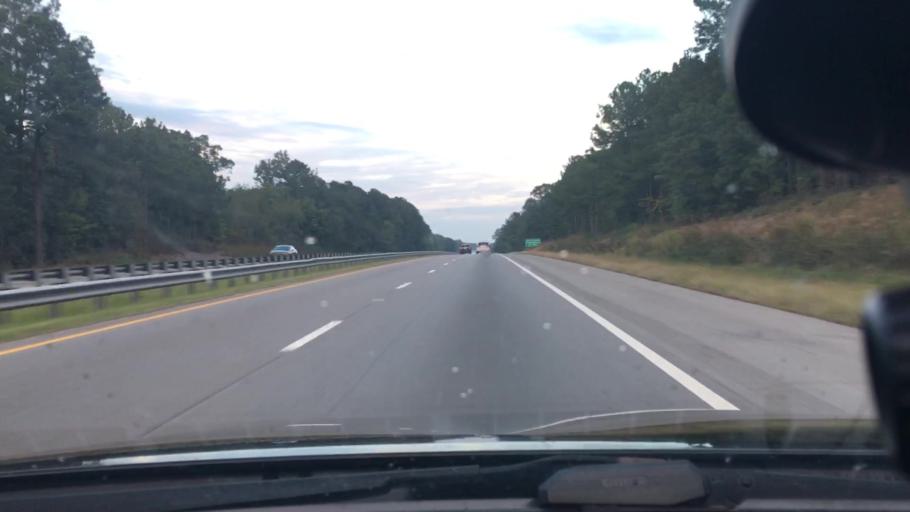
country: US
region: North Carolina
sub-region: Wake County
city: Apex
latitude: 35.6833
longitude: -78.8993
